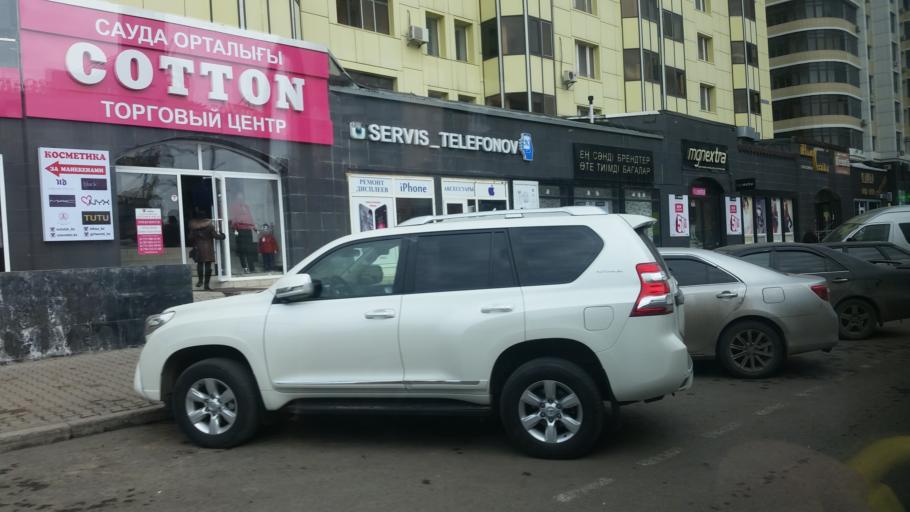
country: KZ
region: Astana Qalasy
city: Astana
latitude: 51.1660
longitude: 71.4293
